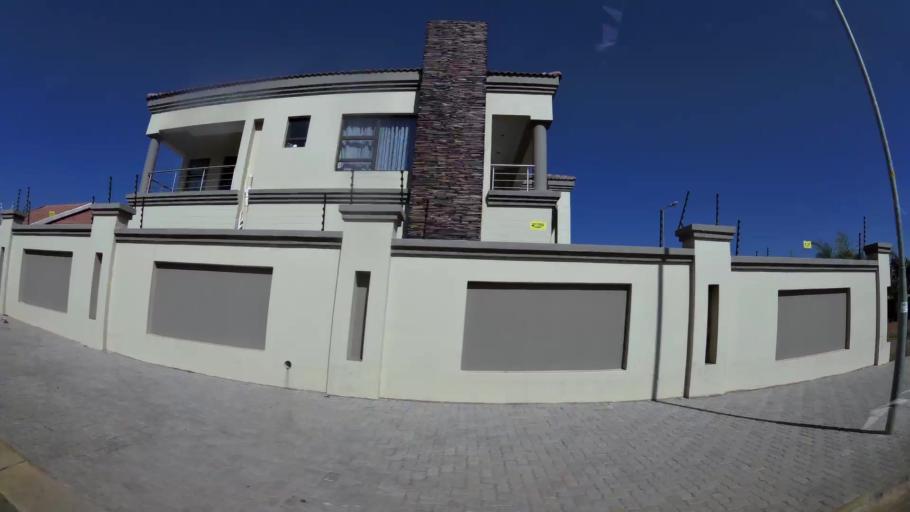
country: ZA
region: Gauteng
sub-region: City of Tshwane Metropolitan Municipality
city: Pretoria
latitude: -25.6513
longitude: 28.2681
